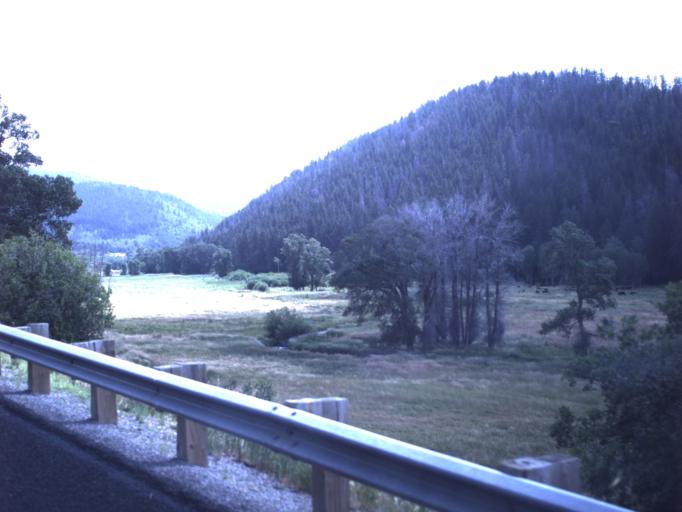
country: US
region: Utah
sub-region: Summit County
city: Francis
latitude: 40.5588
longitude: -111.1290
